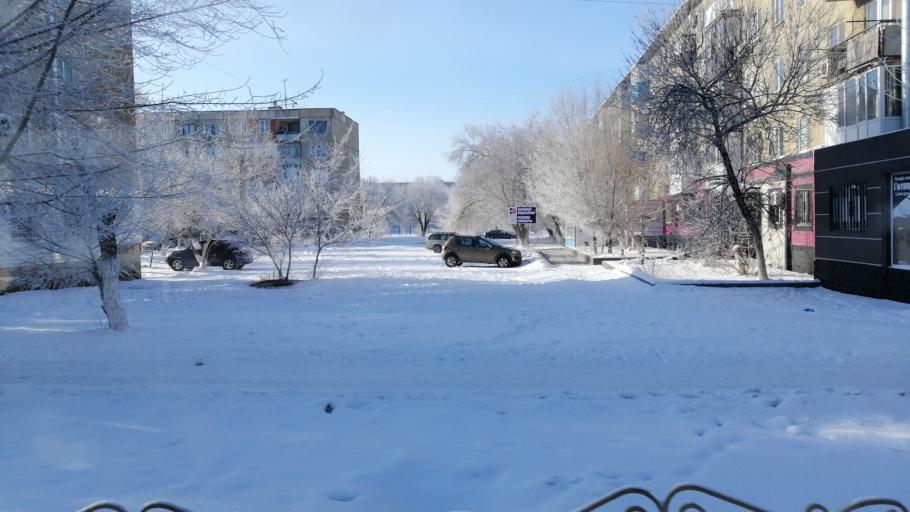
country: KZ
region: Aqtoebe
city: Aqtobe
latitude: 50.3041
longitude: 57.1518
